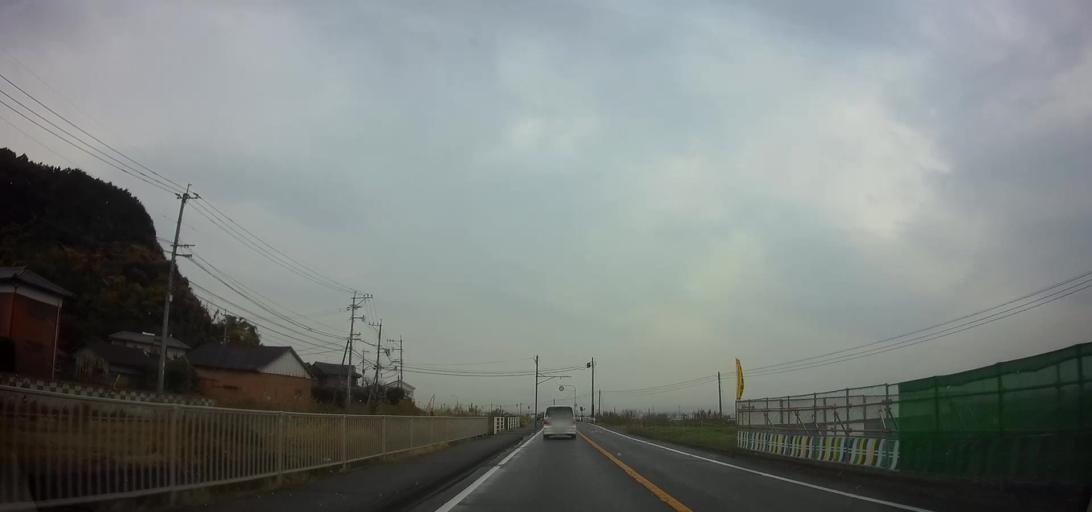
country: JP
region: Nagasaki
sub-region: Isahaya-shi
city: Isahaya
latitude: 32.8373
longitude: 130.1047
